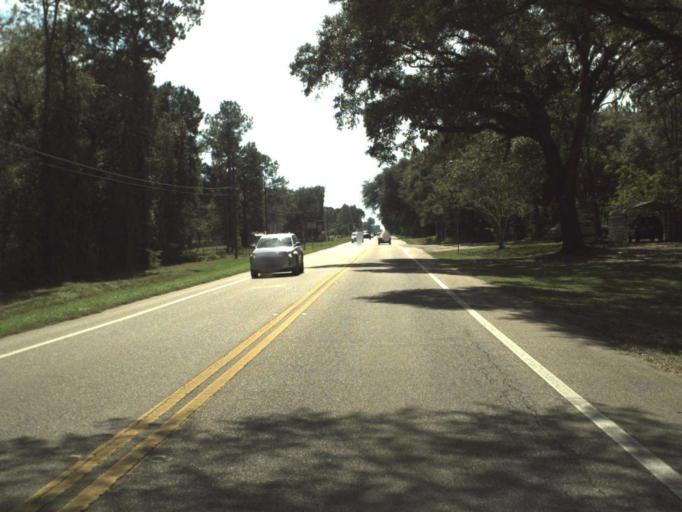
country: US
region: Florida
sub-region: Jackson County
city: Graceville
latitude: 30.9292
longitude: -85.5193
